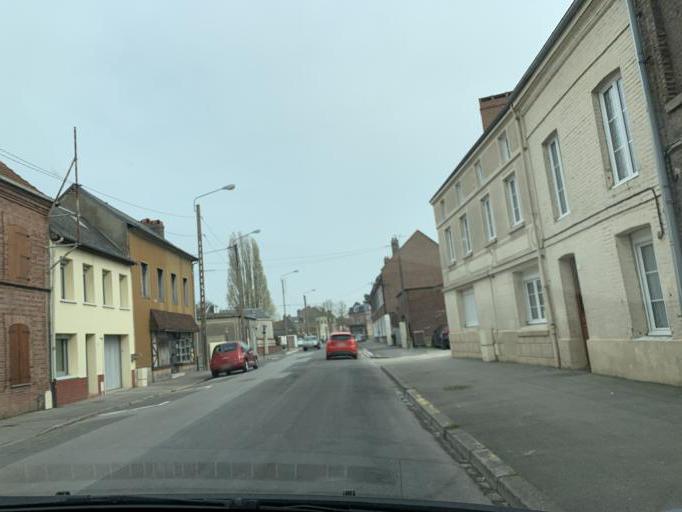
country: FR
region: Picardie
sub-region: Departement de la Somme
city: Abbeville
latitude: 50.1094
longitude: 1.8237
